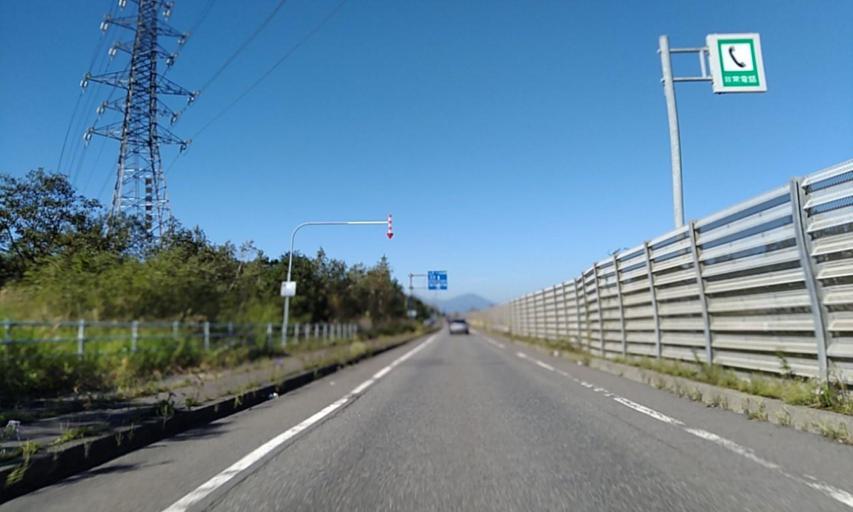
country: JP
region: Hokkaido
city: Tomakomai
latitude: 42.6757
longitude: 141.7235
